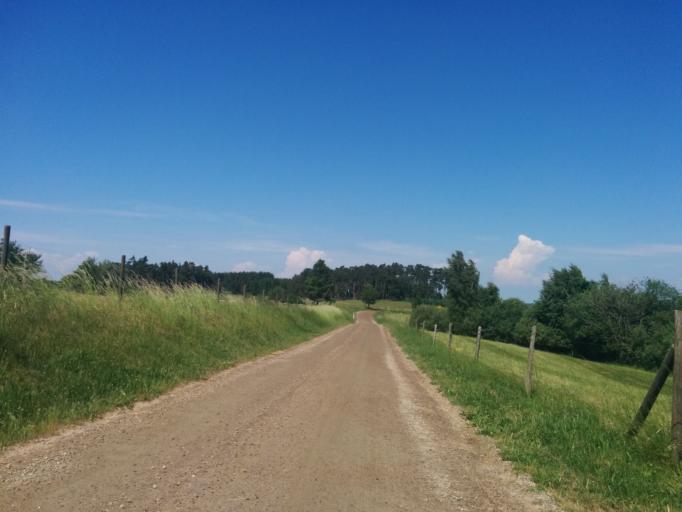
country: SE
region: Skane
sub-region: Lunds Kommun
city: Genarp
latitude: 55.5919
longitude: 13.3829
